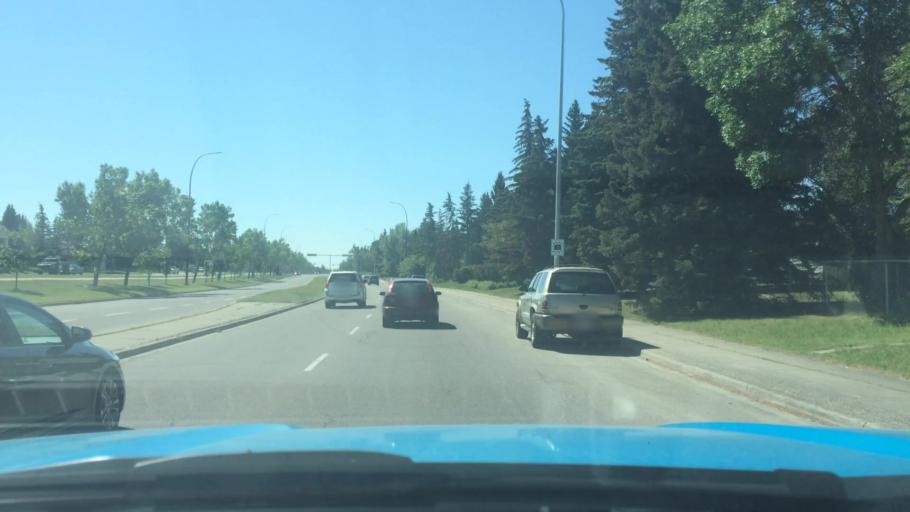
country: CA
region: Alberta
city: Calgary
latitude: 51.0594
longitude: -113.9584
